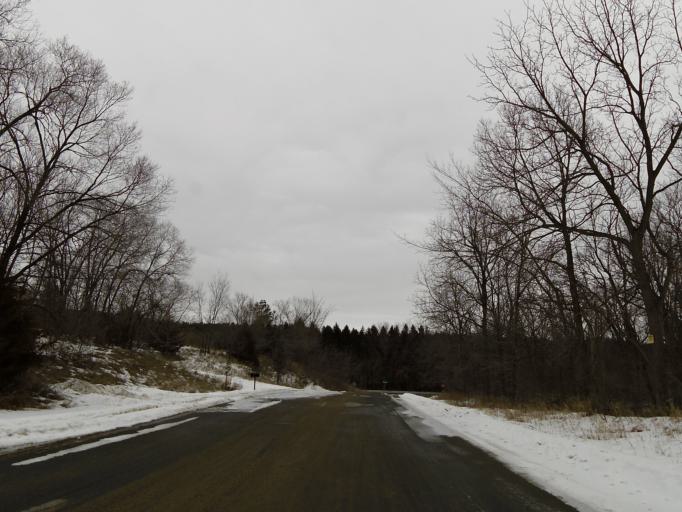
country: US
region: Wisconsin
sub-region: Pierce County
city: Prescott
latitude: 44.7991
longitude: -92.8080
